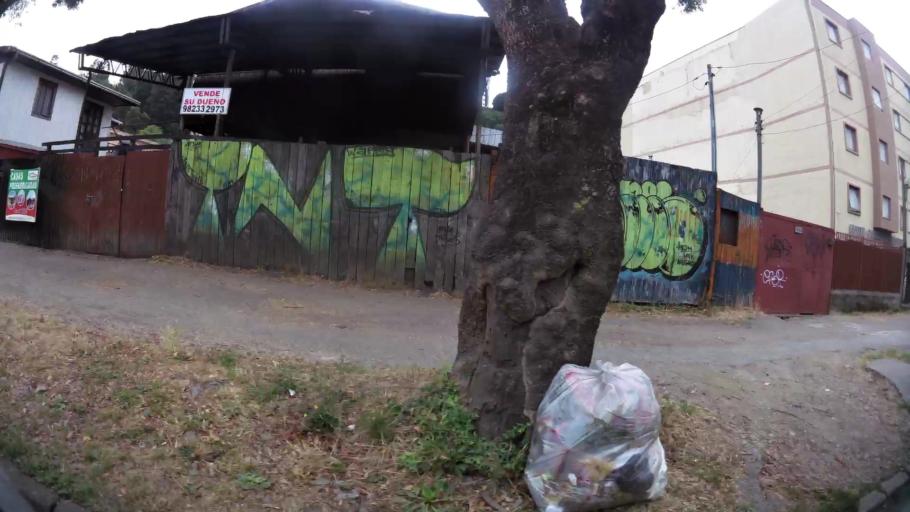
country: CL
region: Biobio
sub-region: Provincia de Concepcion
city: Concepcion
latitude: -36.8102
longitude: -73.0351
